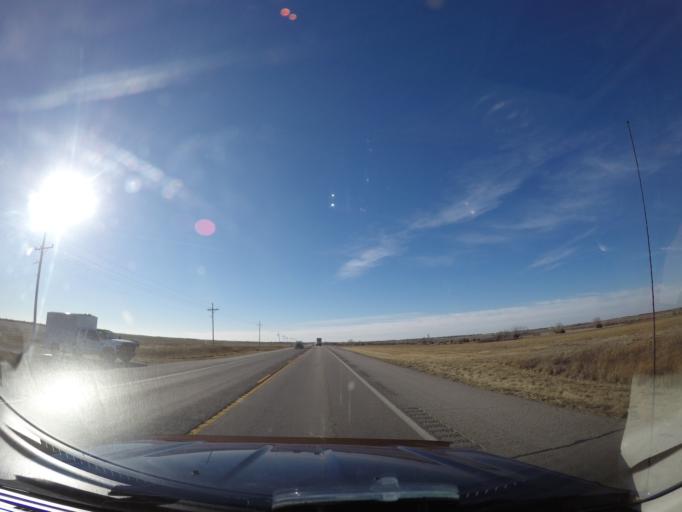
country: US
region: Kansas
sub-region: Marion County
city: Hillsboro
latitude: 38.3626
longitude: -97.2701
